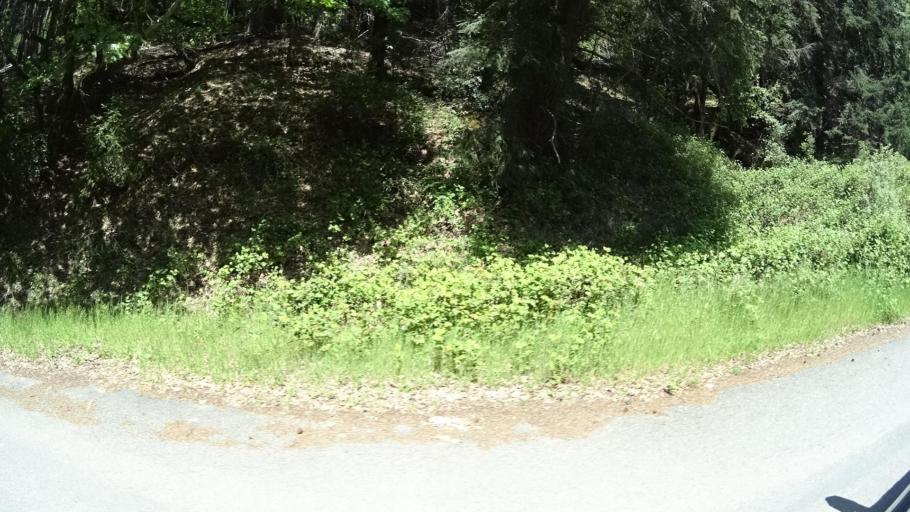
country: US
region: California
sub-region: Humboldt County
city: Redway
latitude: 40.1922
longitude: -123.5385
